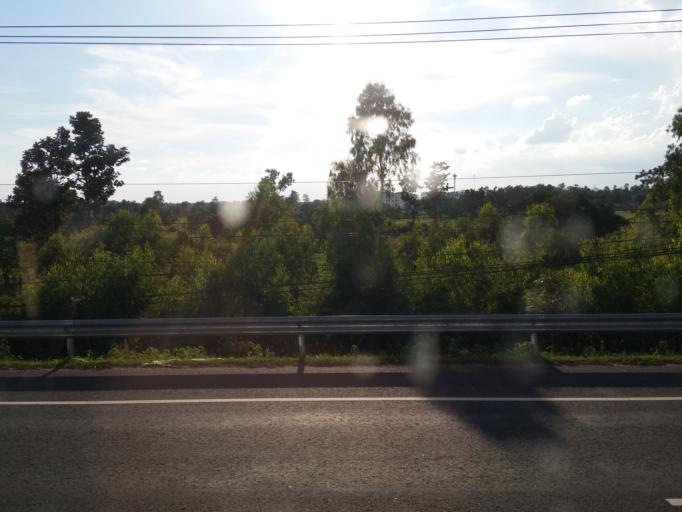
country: TH
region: Changwat Ubon Ratchathani
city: Sirindhorn
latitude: 15.1915
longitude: 105.3678
